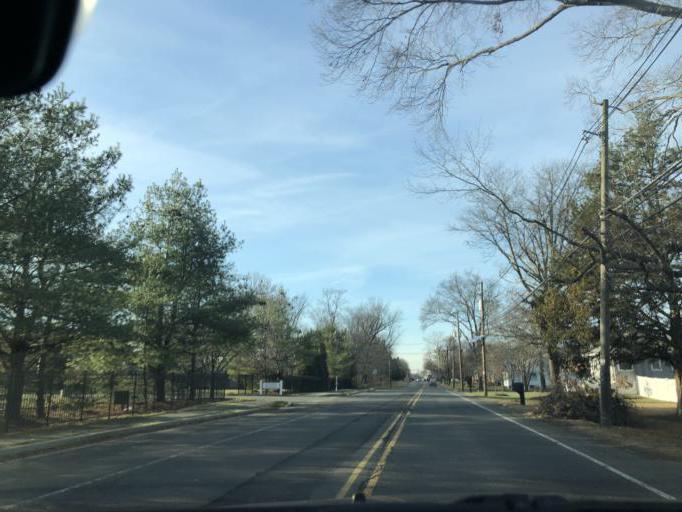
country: US
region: New Jersey
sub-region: Burlington County
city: Moorestown-Lenola
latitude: 39.9691
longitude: -74.9648
